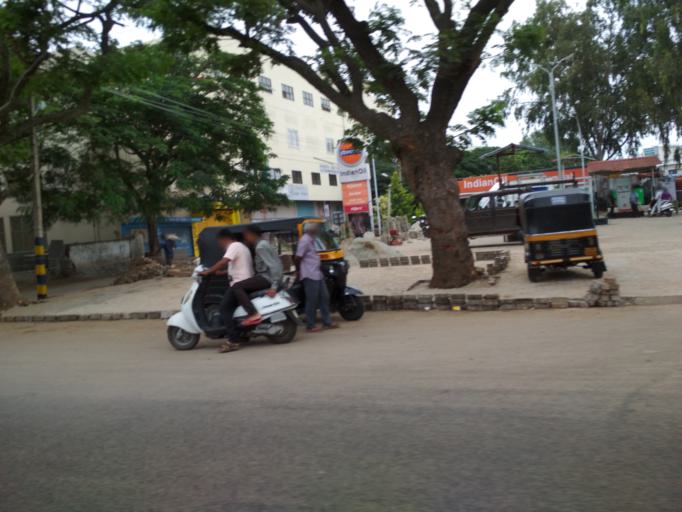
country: IN
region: Karnataka
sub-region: Mysore
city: Mysore
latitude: 12.3186
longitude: 76.6489
